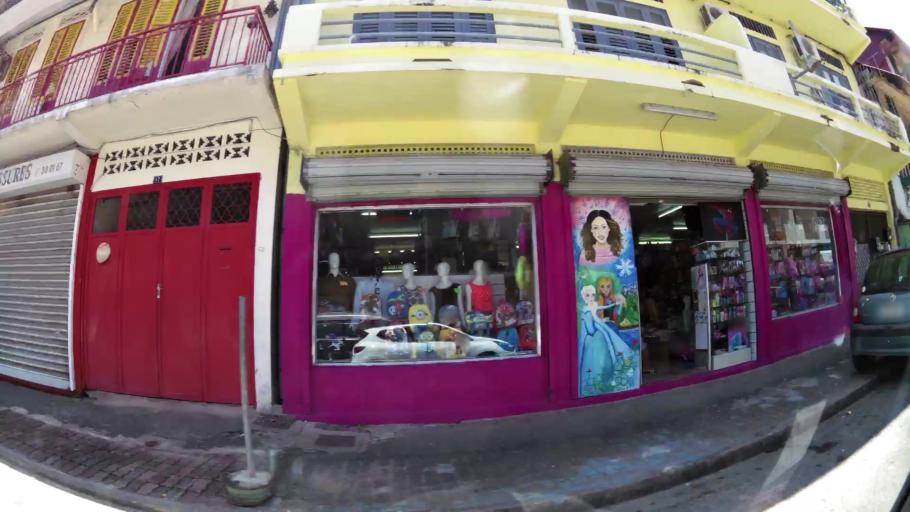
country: GF
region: Guyane
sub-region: Guyane
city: Cayenne
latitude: 4.9377
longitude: -52.3333
